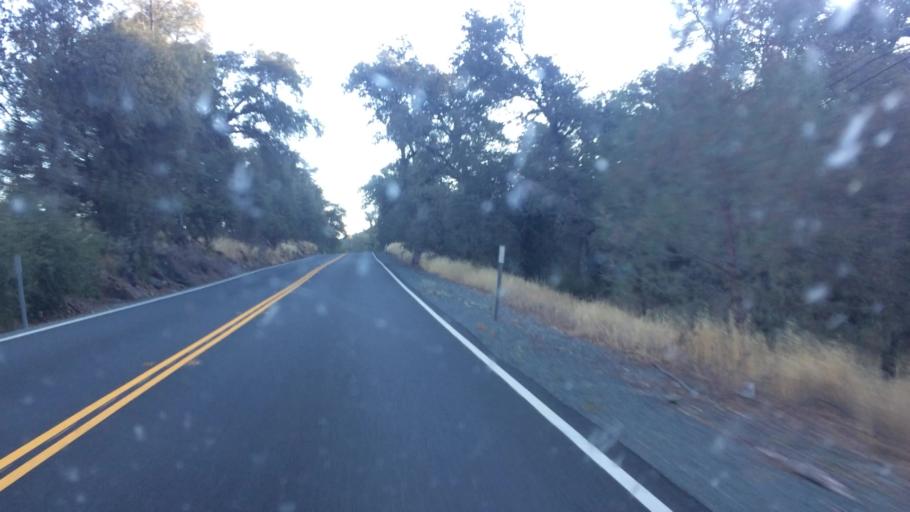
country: US
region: California
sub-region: Amador County
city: Plymouth
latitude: 38.5607
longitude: -120.8469
